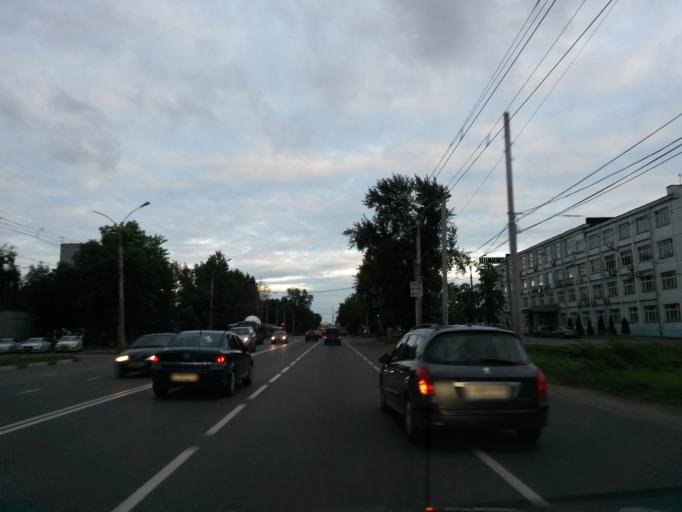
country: RU
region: Jaroslavl
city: Yaroslavl
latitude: 57.6488
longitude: 39.8491
